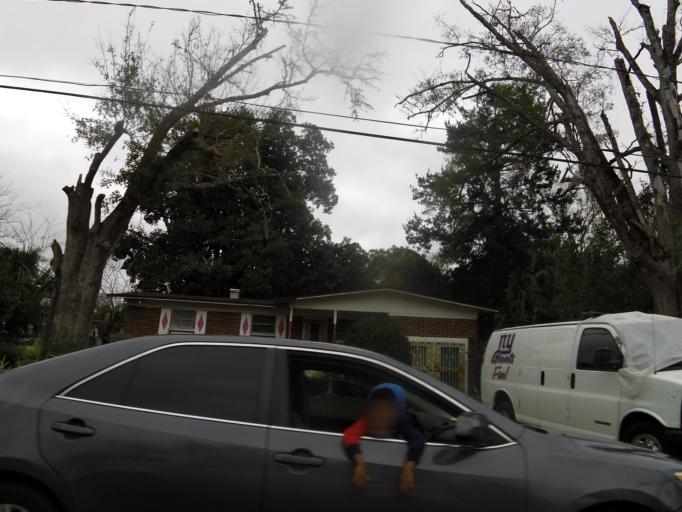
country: US
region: Florida
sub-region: Duval County
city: Jacksonville
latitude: 30.3716
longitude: -81.7100
